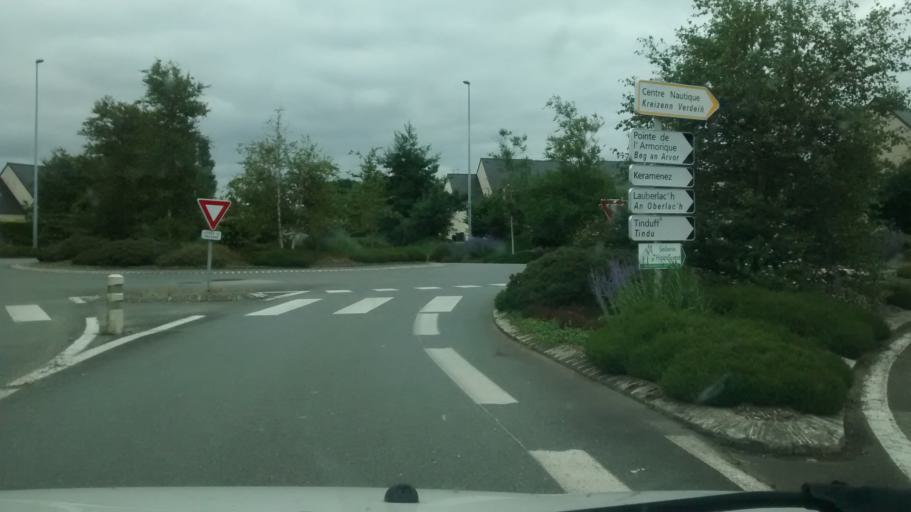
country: FR
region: Brittany
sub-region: Departement du Finistere
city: Plougastel-Daoulas
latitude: 48.3678
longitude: -4.3724
